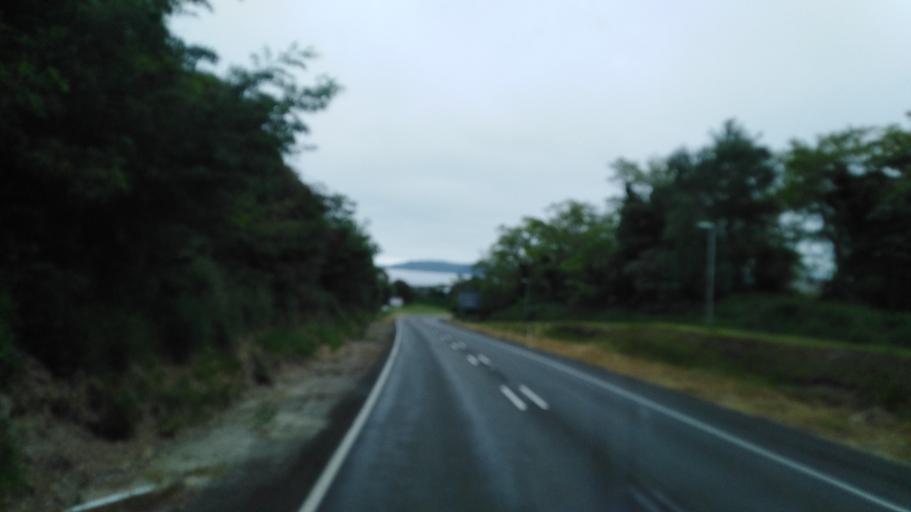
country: NZ
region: Waikato
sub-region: Taupo District
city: Taupo
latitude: -38.7049
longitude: 176.0939
